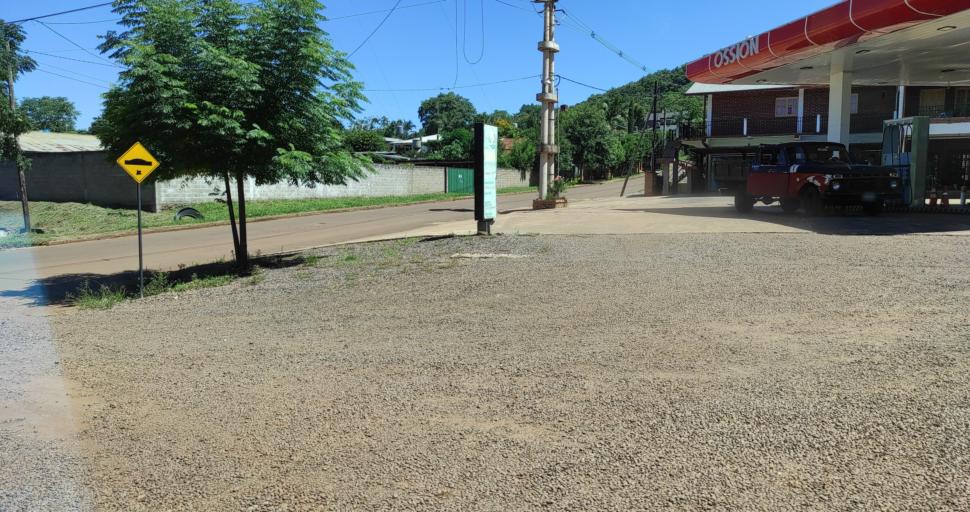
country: AR
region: Misiones
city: El Soberbio
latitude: -27.2933
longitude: -54.2042
